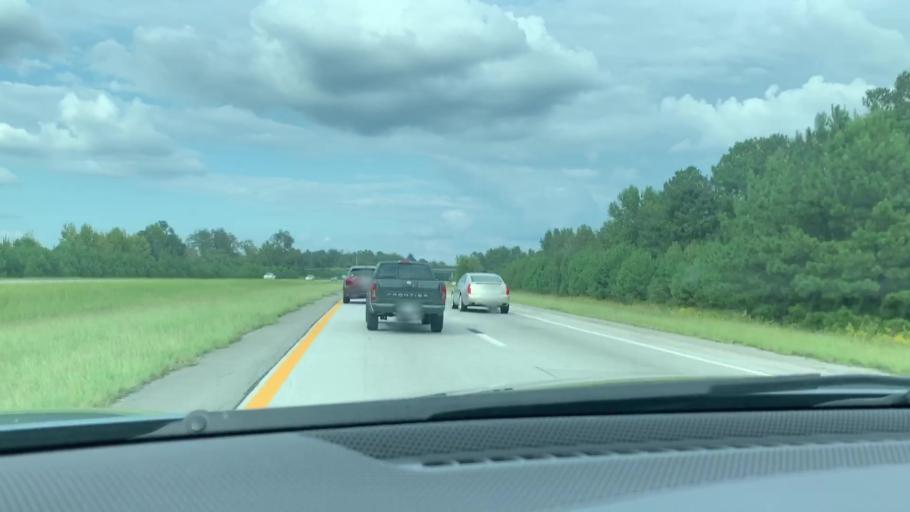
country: US
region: South Carolina
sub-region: Dorchester County
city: Saint George
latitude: 33.1262
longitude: -80.6395
